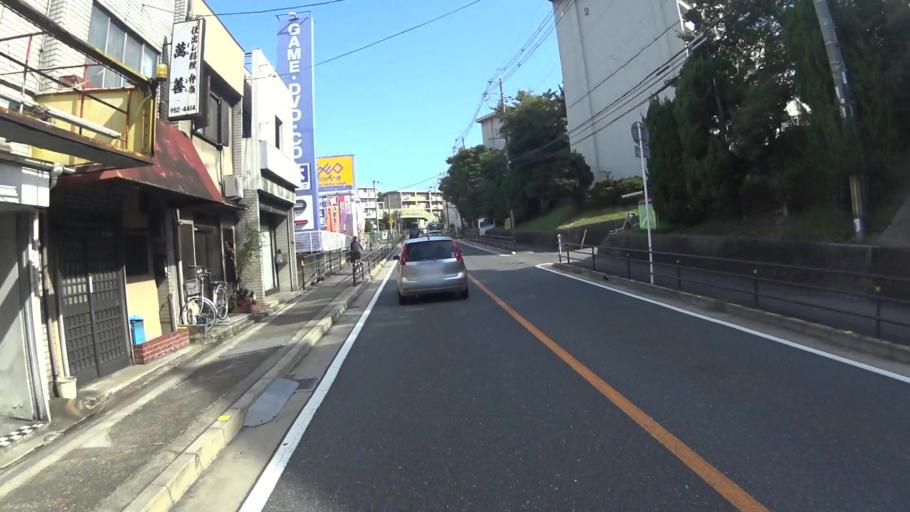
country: JP
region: Kyoto
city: Muko
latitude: 34.9447
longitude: 135.6957
